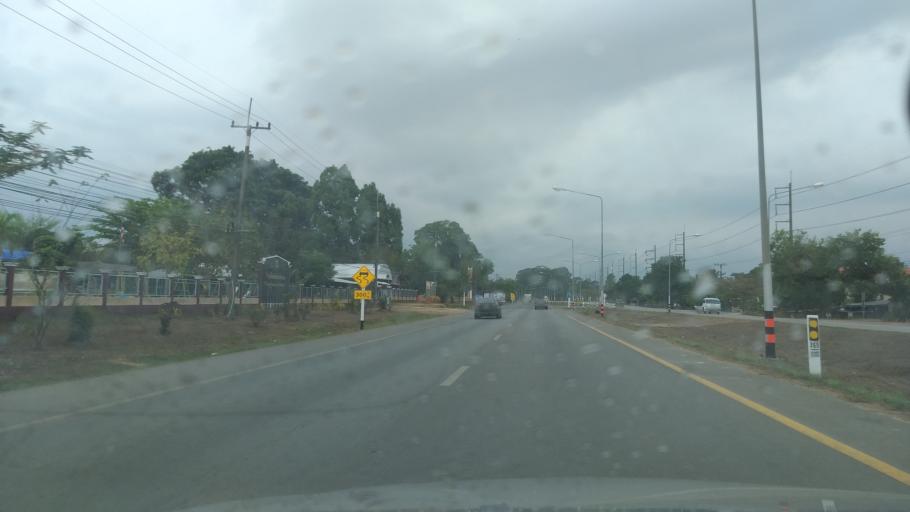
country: TH
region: Chanthaburi
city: Khlung
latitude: 12.4277
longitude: 102.3166
